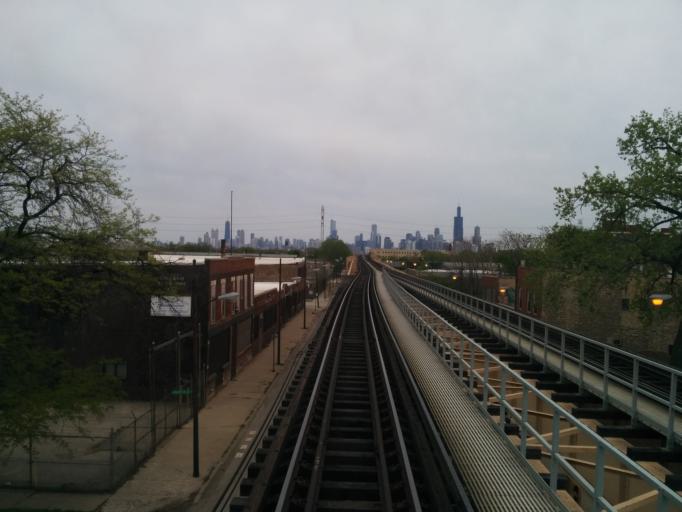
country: US
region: Illinois
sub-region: Cook County
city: Chicago
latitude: 41.8839
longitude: -87.6955
